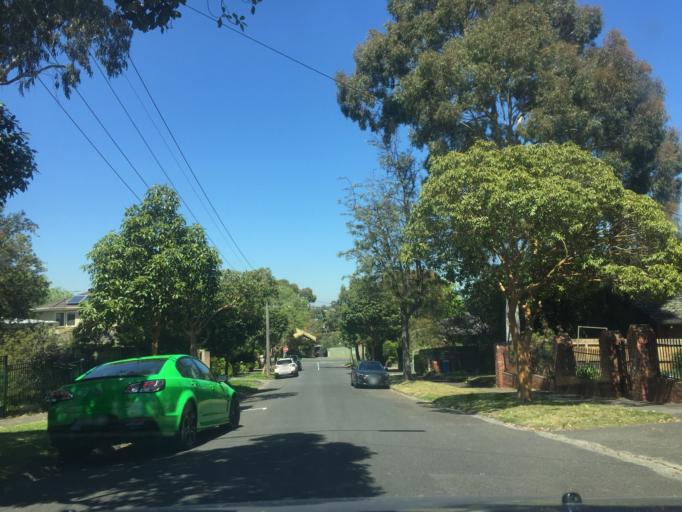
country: AU
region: Victoria
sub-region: Boroondara
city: Canterbury
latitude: -37.8186
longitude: 145.0899
